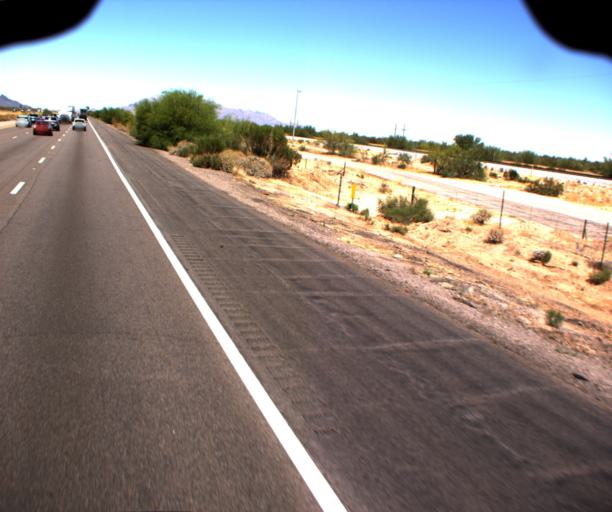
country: US
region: Arizona
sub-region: Pima County
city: Avra Valley
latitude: 32.5539
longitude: -111.3065
